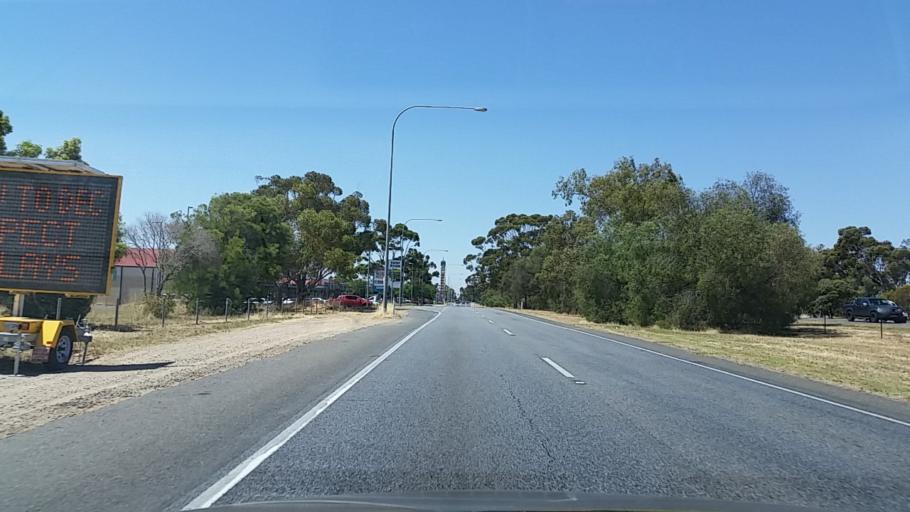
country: AU
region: South Australia
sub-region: Playford
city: Smithfield
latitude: -34.6937
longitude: 138.6868
